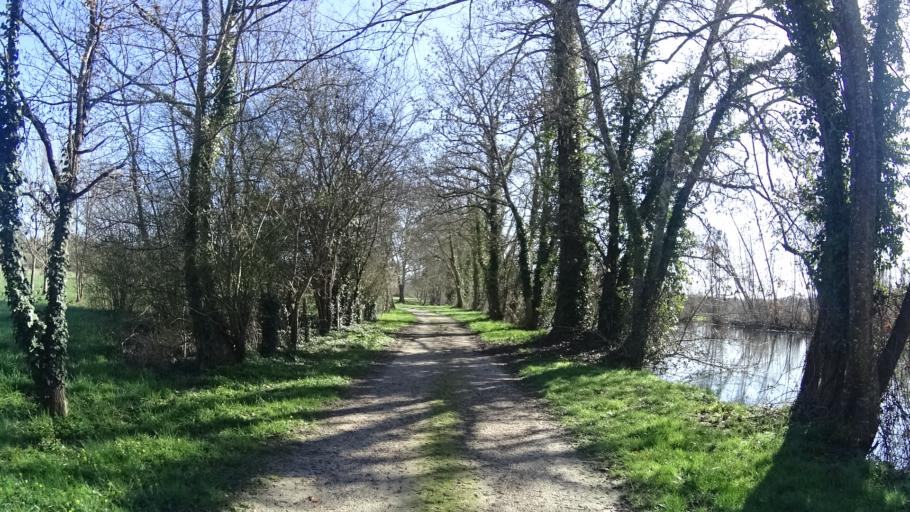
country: FR
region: Aquitaine
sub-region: Departement de la Dordogne
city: Saint-Aulaye
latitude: 45.2203
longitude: 0.1059
